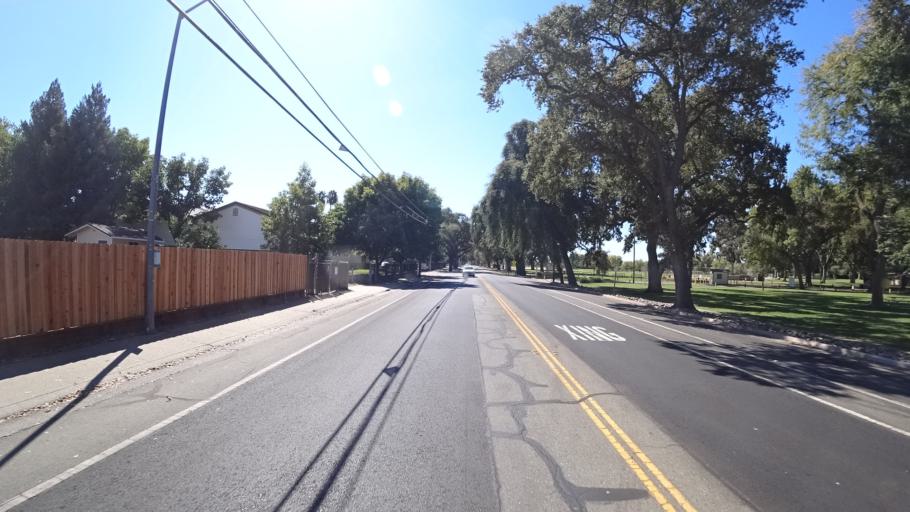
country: US
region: California
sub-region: Sacramento County
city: Elk Grove
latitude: 38.3971
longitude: -121.3714
